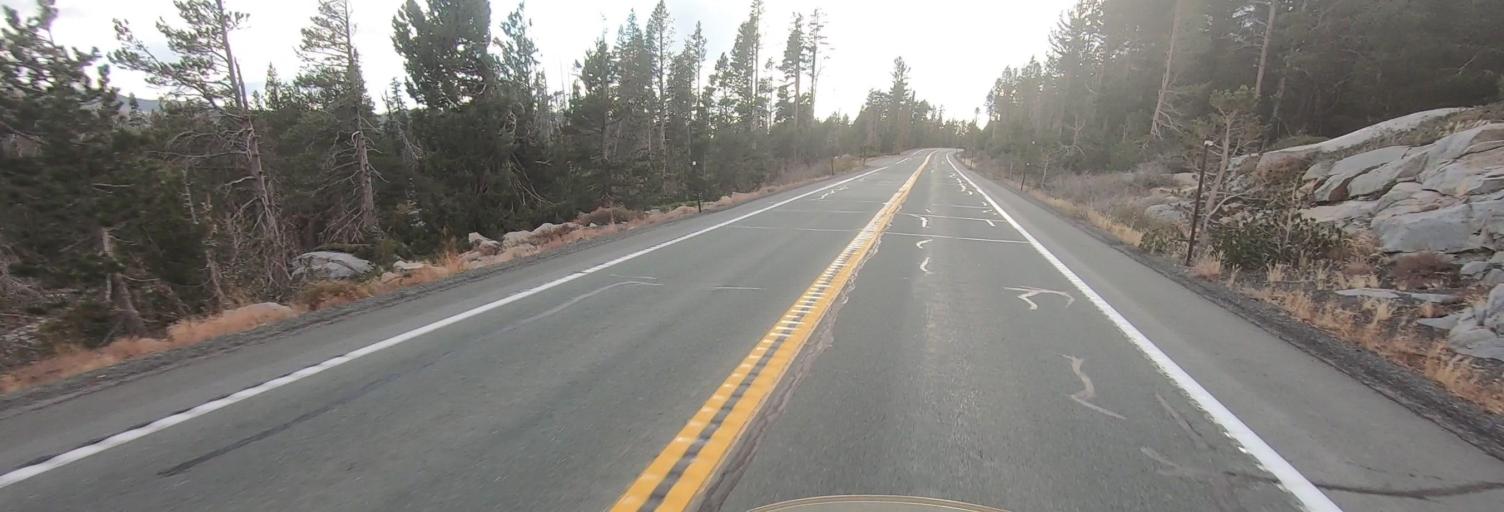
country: US
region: California
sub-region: El Dorado County
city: South Lake Tahoe
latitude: 38.6344
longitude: -120.1549
